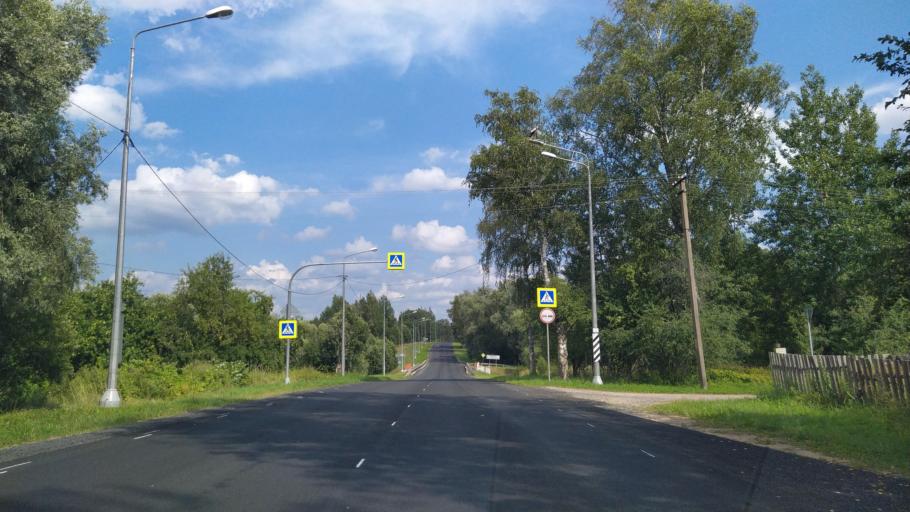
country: RU
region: Pskov
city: Porkhov
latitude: 57.7310
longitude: 29.3839
